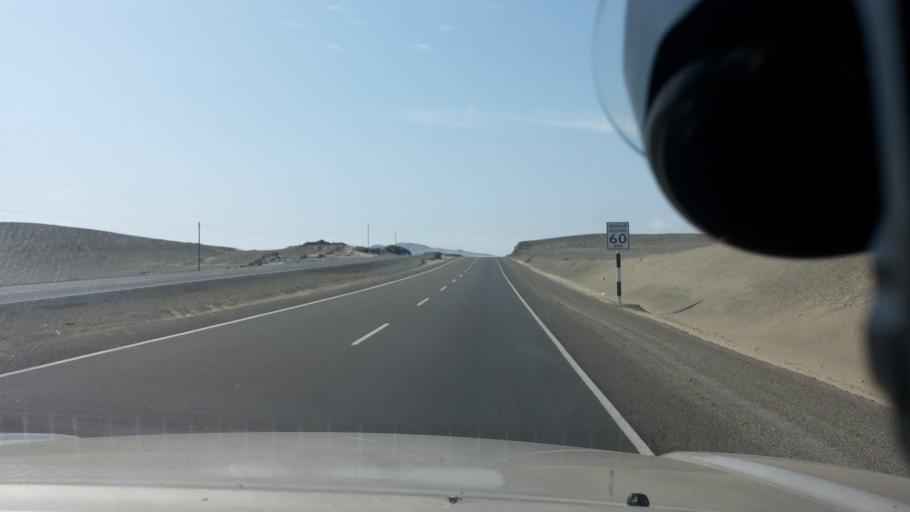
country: PE
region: Ancash
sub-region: Provincia de Huarmey
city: La Caleta Culebras
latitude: -9.7712
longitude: -78.2346
